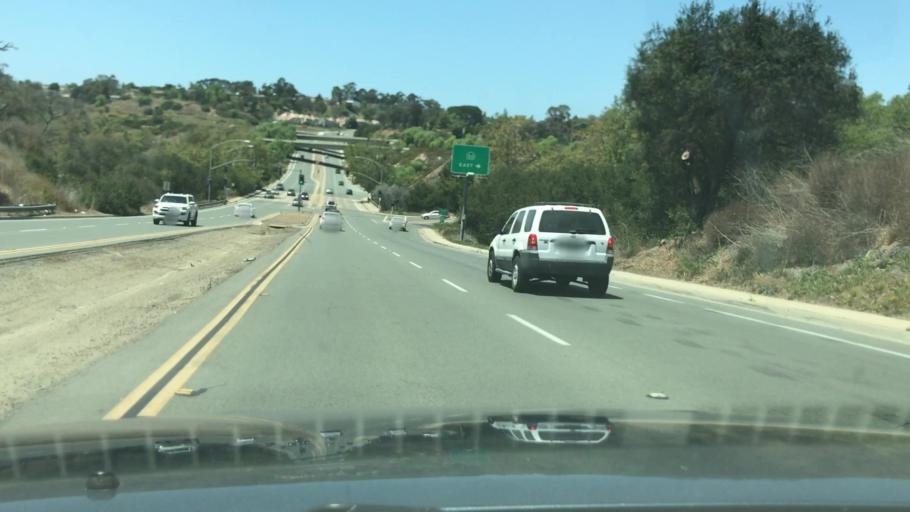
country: US
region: California
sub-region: San Diego County
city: La Jolla
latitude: 32.8439
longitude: -117.1987
